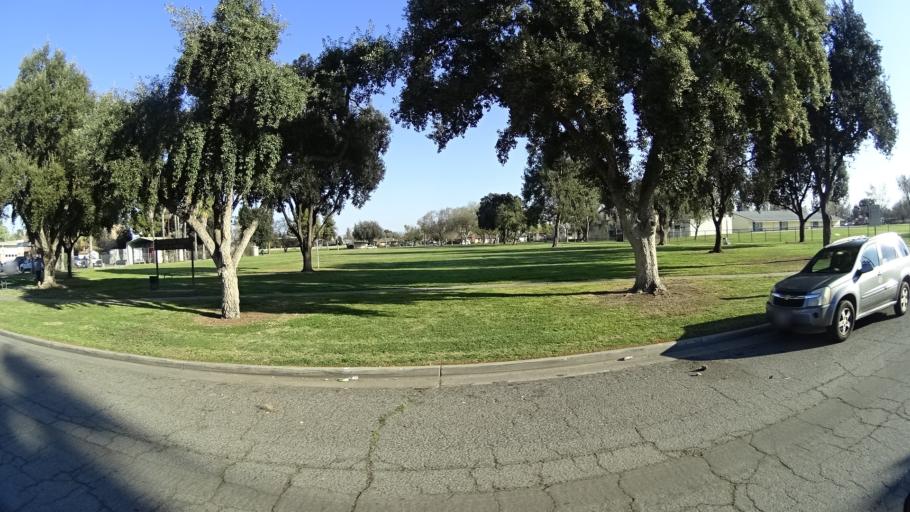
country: US
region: California
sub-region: Fresno County
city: Fresno
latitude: 36.8176
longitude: -119.7797
